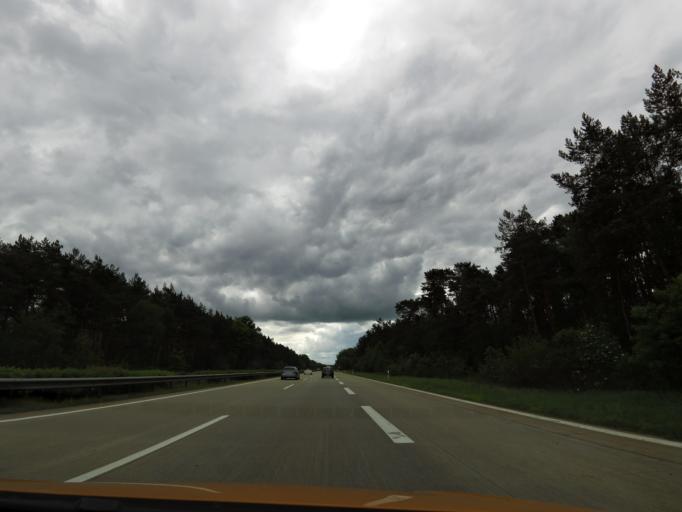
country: DE
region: Lower Saxony
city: Walsrode
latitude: 52.8265
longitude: 9.6070
